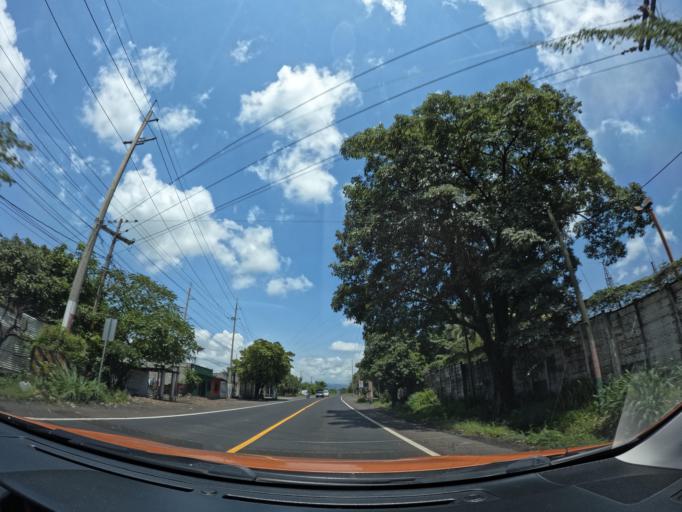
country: GT
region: Escuintla
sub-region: Municipio de Masagua
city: Masagua
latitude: 14.2368
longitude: -90.8196
